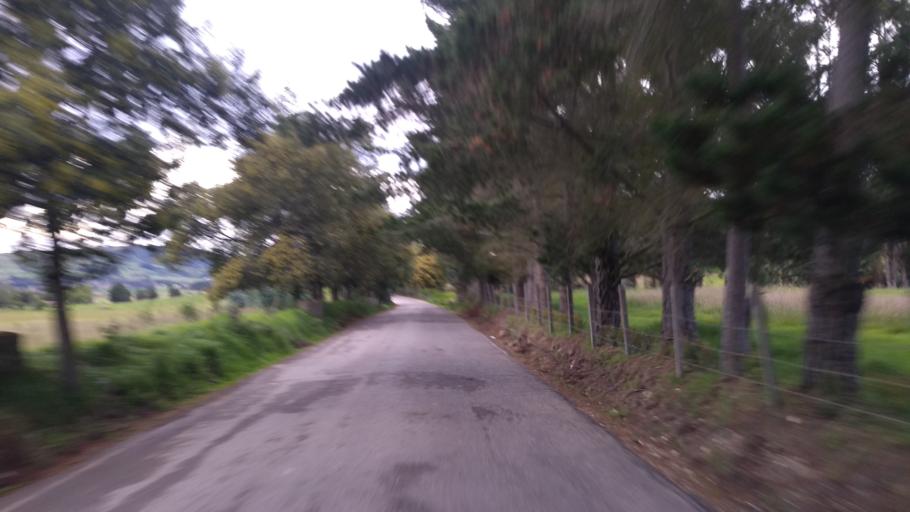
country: CO
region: Boyaca
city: Toca
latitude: 5.5961
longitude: -73.1798
